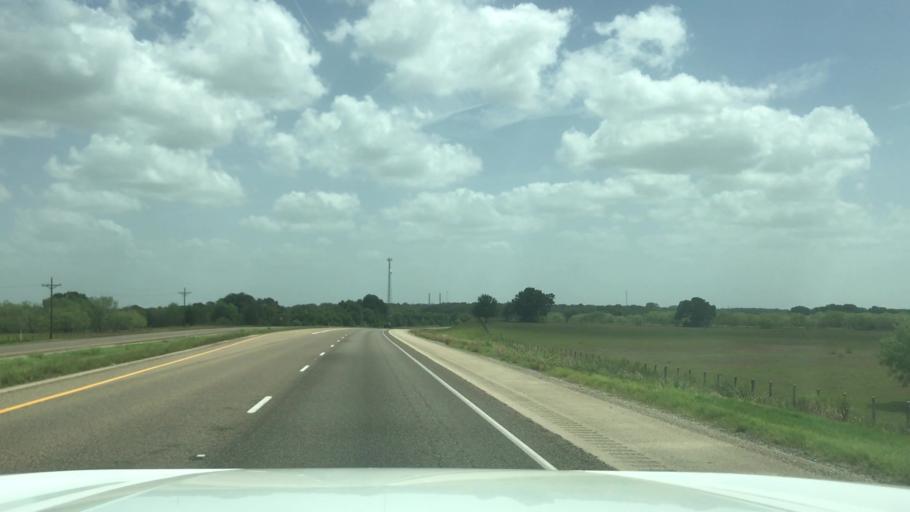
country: US
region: Texas
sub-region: Robertson County
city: Calvert
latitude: 31.1266
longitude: -96.7150
